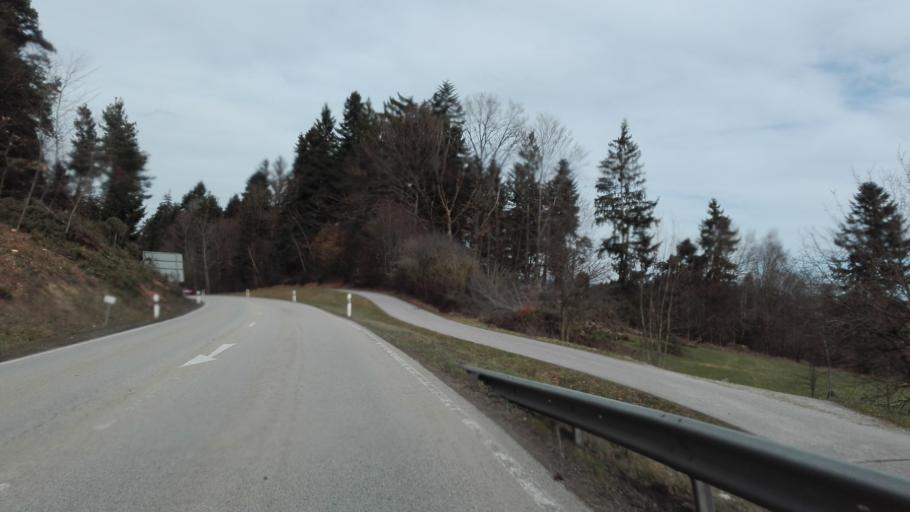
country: DE
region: Bavaria
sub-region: Lower Bavaria
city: Thyrnau
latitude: 48.5992
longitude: 13.5349
